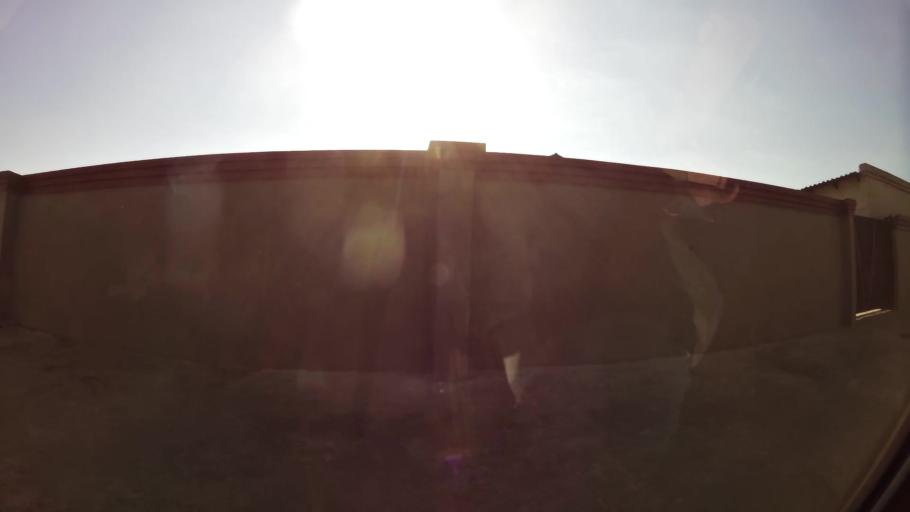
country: ZA
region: Gauteng
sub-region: City of Johannesburg Metropolitan Municipality
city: Soweto
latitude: -26.2469
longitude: 27.9296
